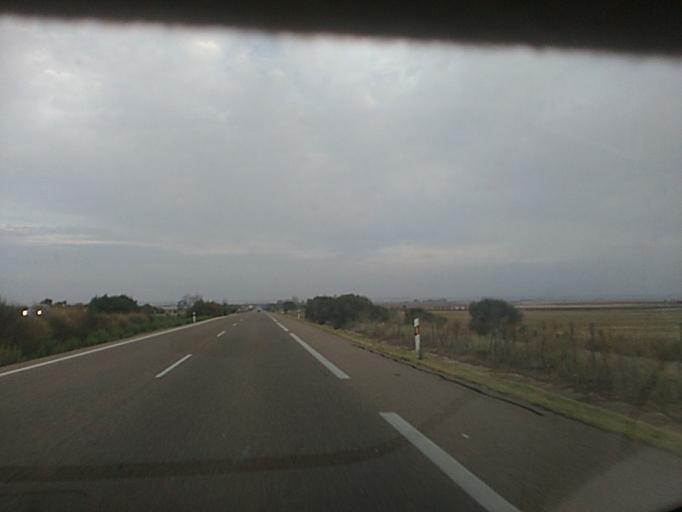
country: ES
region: Castille and Leon
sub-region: Provincia de Zamora
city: Villalpando
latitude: 41.8364
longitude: -5.3878
